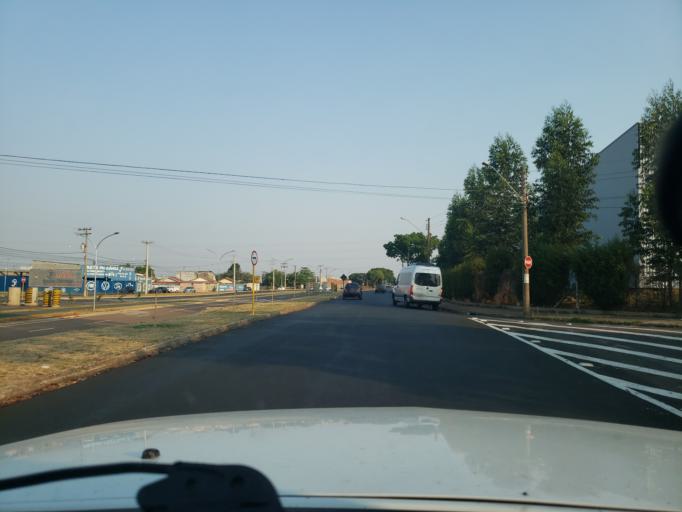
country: BR
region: Sao Paulo
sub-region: Moji-Guacu
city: Mogi-Gaucu
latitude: -22.3378
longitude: -46.9440
